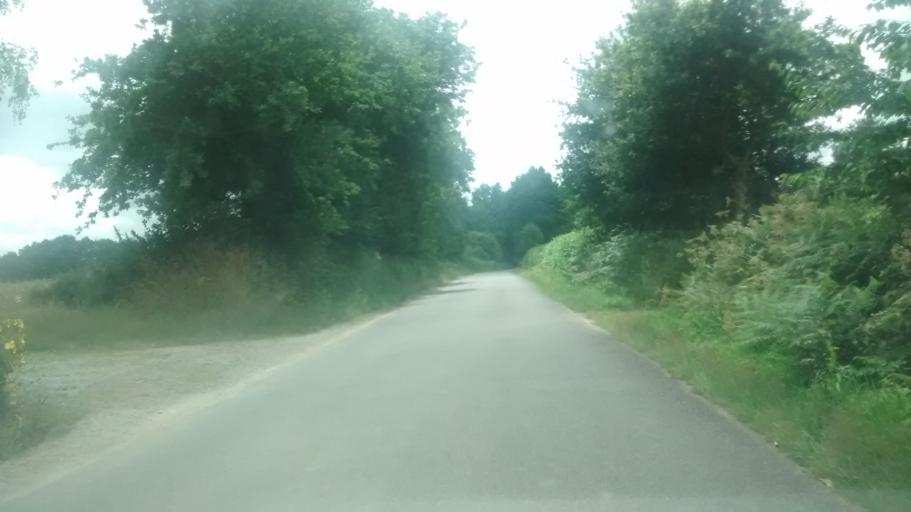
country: FR
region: Brittany
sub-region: Departement du Morbihan
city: Molac
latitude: 47.7865
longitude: -2.4386
